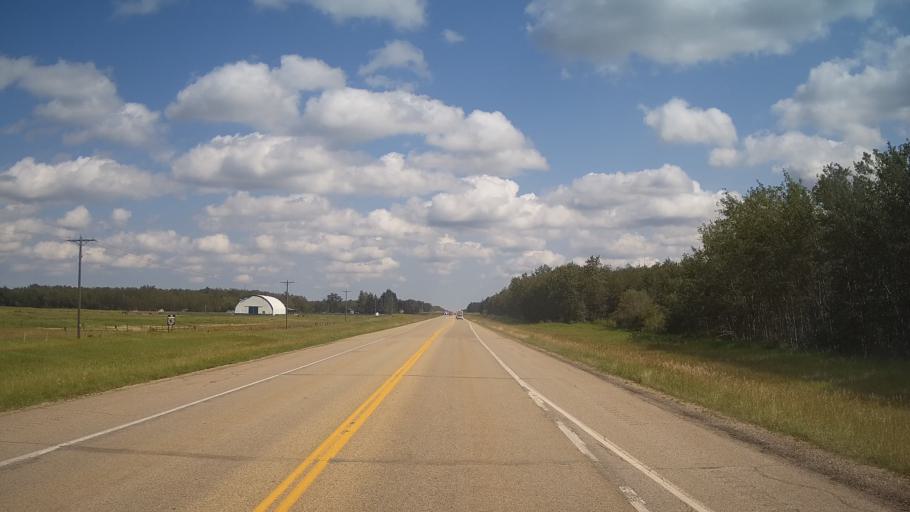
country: CA
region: Alberta
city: Sherwood Park
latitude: 53.3957
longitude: -113.0729
